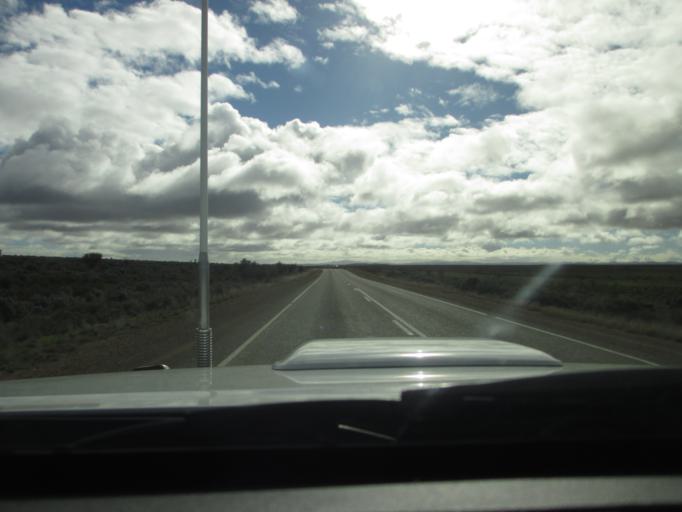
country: AU
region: South Australia
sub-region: Flinders Ranges
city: Quorn
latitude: -32.1843
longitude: 138.5372
